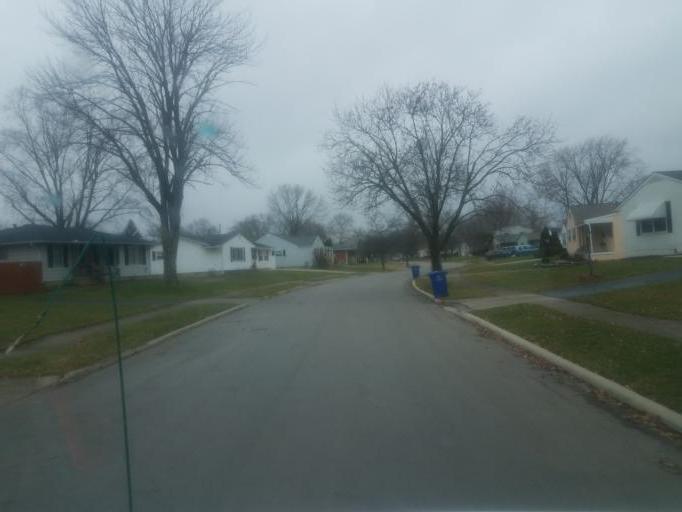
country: US
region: Ohio
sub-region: Franklin County
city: Worthington
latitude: 40.0987
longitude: -82.9786
